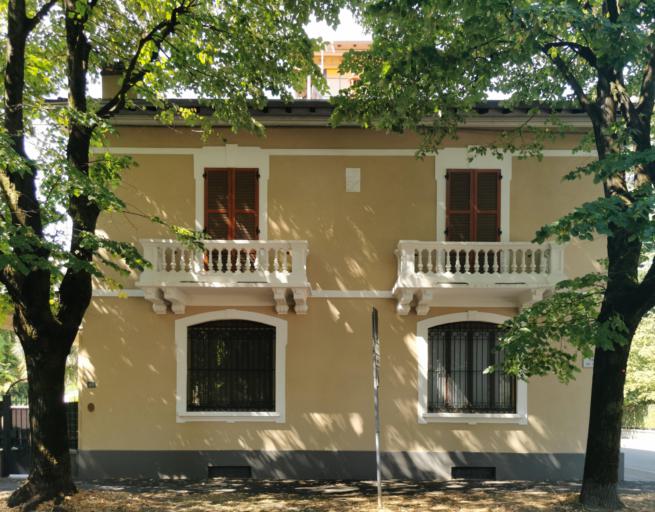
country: IT
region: Lombardy
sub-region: Citta metropolitana di Milano
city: Cusano Milanino
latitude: 45.5537
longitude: 9.1907
